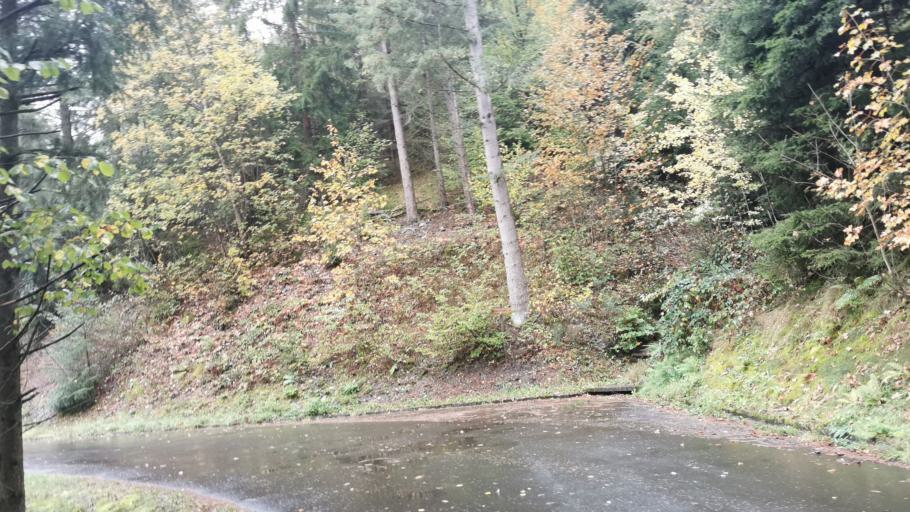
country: DE
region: Bavaria
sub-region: Upper Franconia
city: Nordhalben
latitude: 50.3354
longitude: 11.4928
